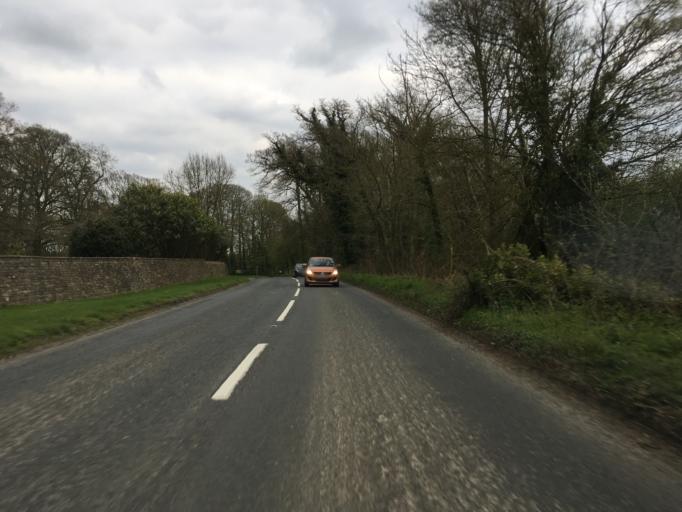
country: GB
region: England
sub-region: Gloucestershire
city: Cirencester
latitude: 51.7466
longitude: -1.8852
